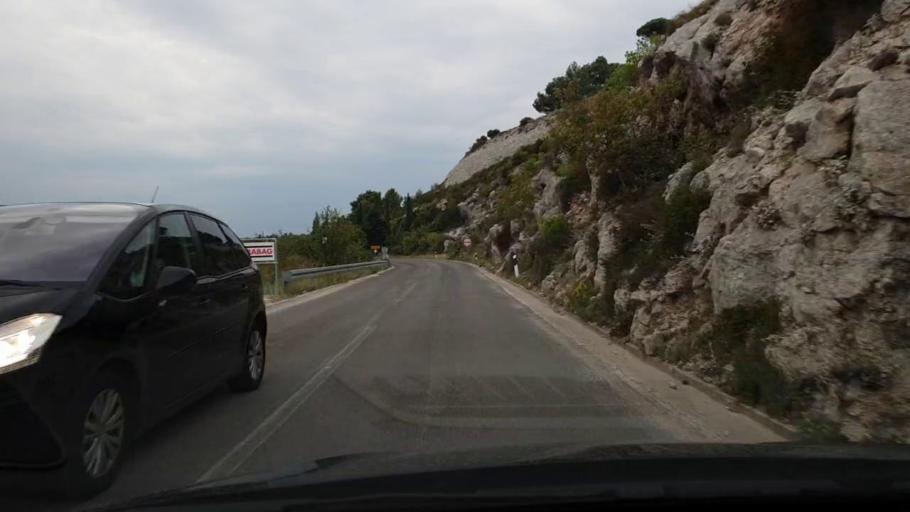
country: HR
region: Dubrovacko-Neretvanska
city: Cibaca
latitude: 42.6492
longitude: 18.1593
